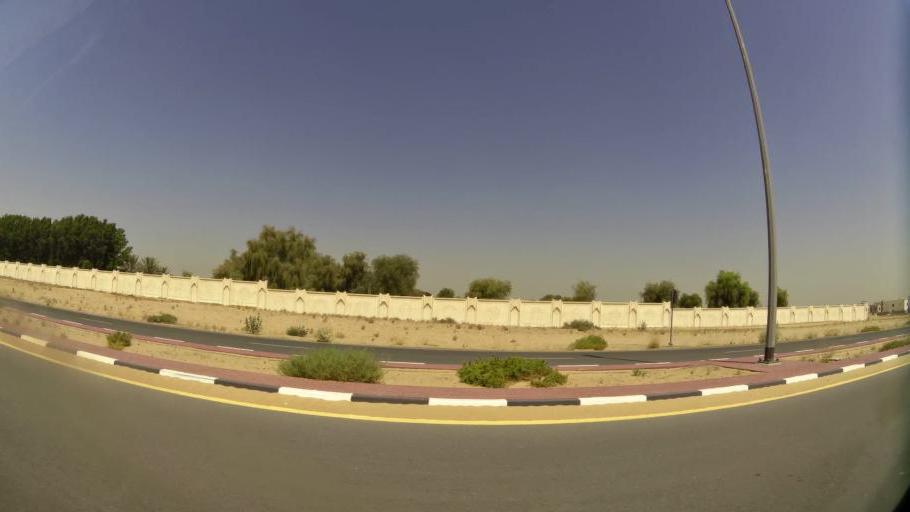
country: AE
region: Ajman
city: Ajman
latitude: 25.4005
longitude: 55.5376
